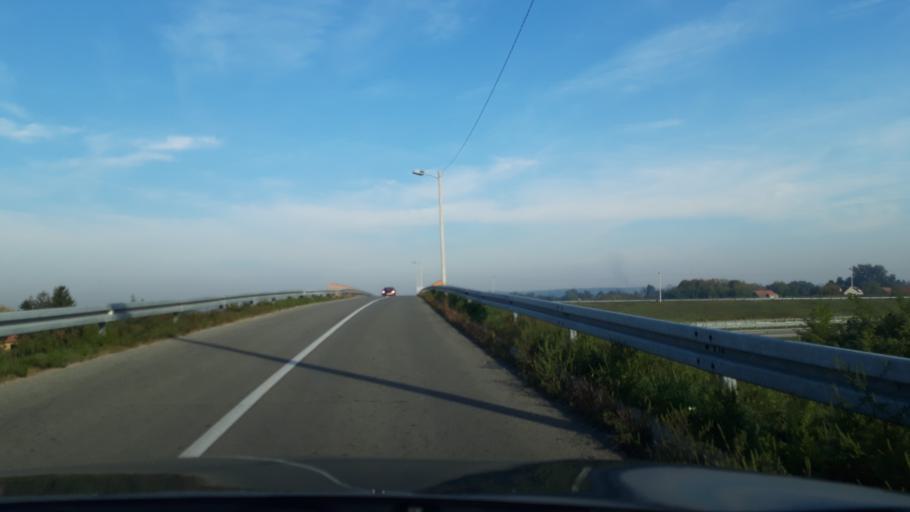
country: HU
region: Csongrad
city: Morahalom
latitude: 46.1276
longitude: 19.8523
